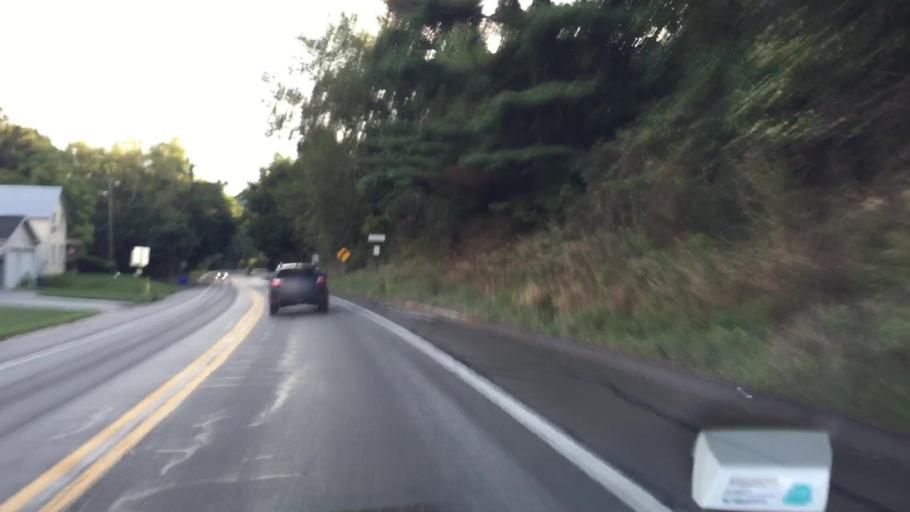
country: US
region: Pennsylvania
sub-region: Butler County
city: Evans City
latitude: 40.7727
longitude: -80.0559
